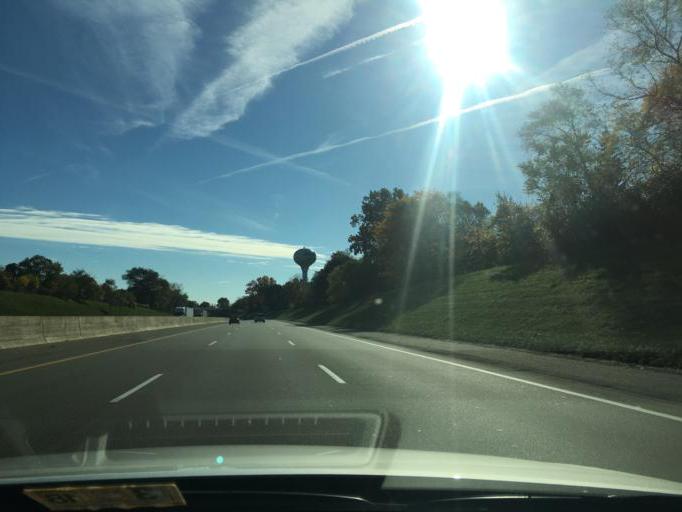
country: US
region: Michigan
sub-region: Wayne County
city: Plymouth
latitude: 42.3885
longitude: -83.4536
